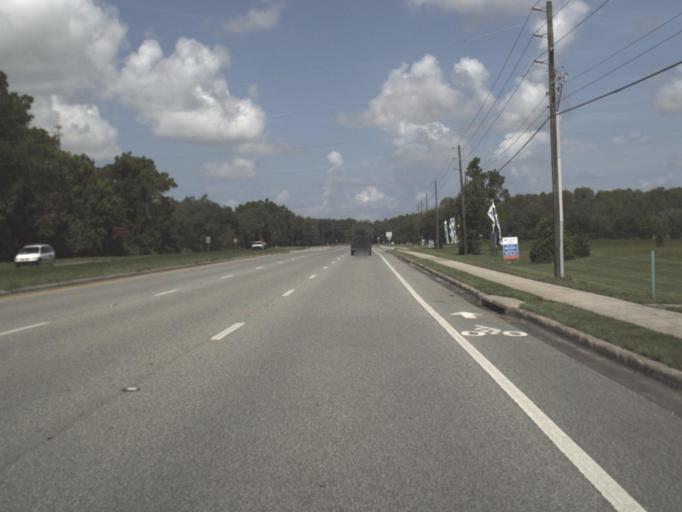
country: US
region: Florida
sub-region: Pasco County
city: Shady Hills
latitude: 28.3293
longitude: -82.5862
